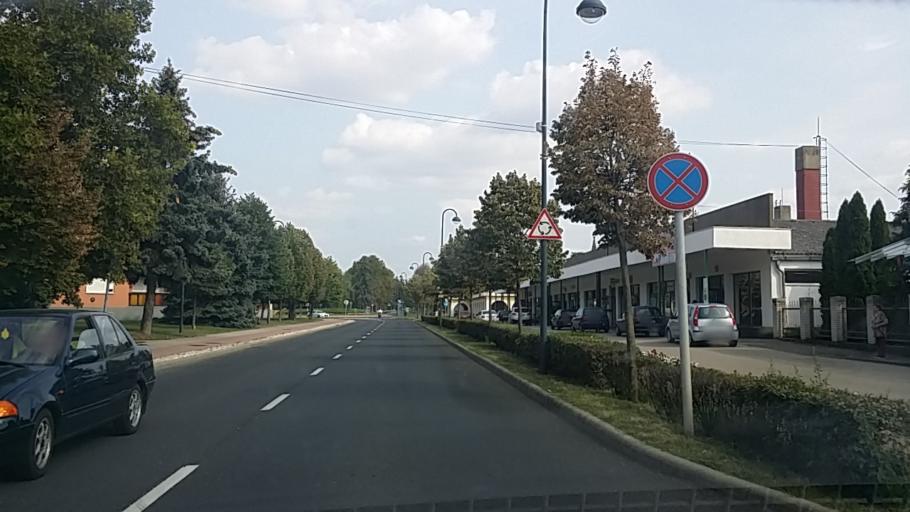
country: HU
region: Komarom-Esztergom
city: Babolna
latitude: 47.6427
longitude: 17.9766
